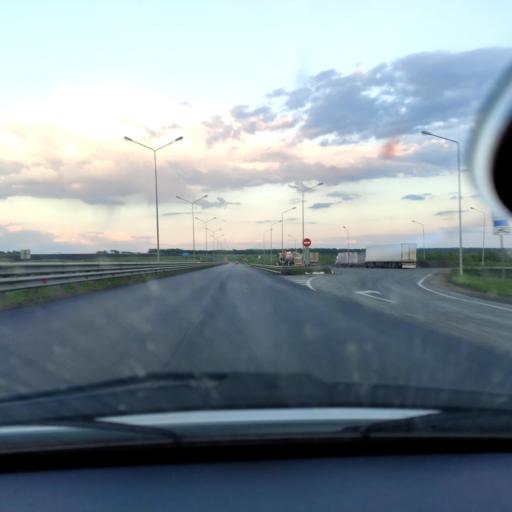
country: RU
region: Bashkortostan
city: Kushnarenkovo
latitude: 55.0718
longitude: 55.2894
